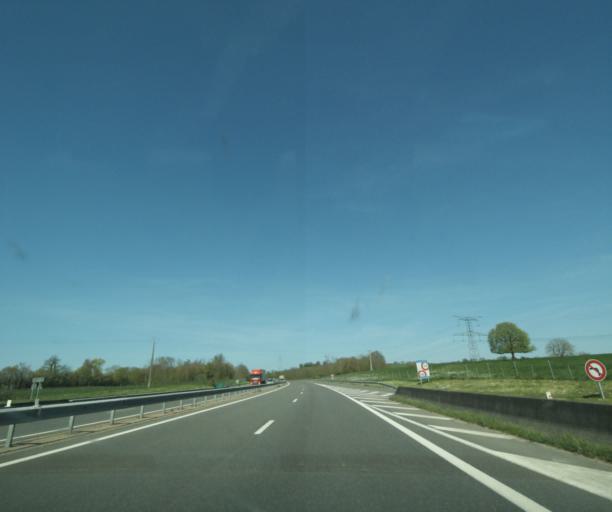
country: FR
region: Bourgogne
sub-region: Departement de la Nievre
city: Pougues-les-Eaux
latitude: 47.0752
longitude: 3.1269
